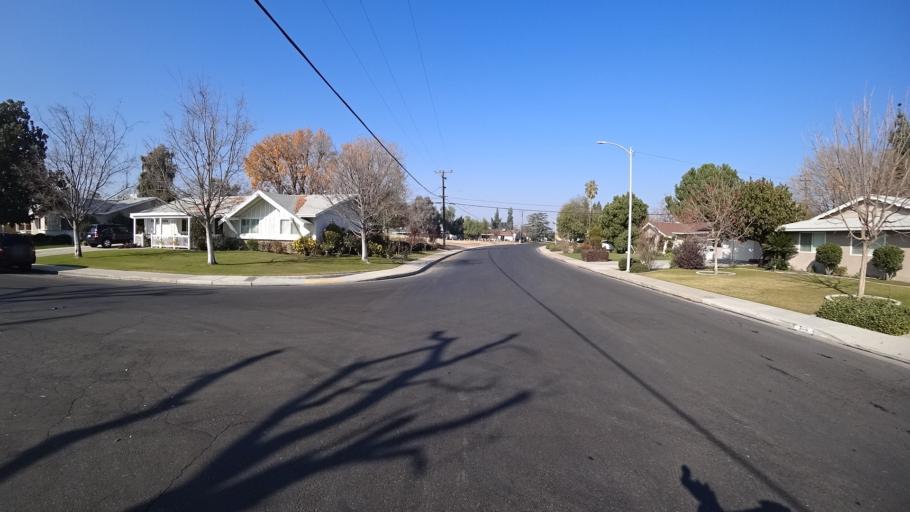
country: US
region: California
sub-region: Kern County
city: Bakersfield
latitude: 35.3518
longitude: -119.0669
